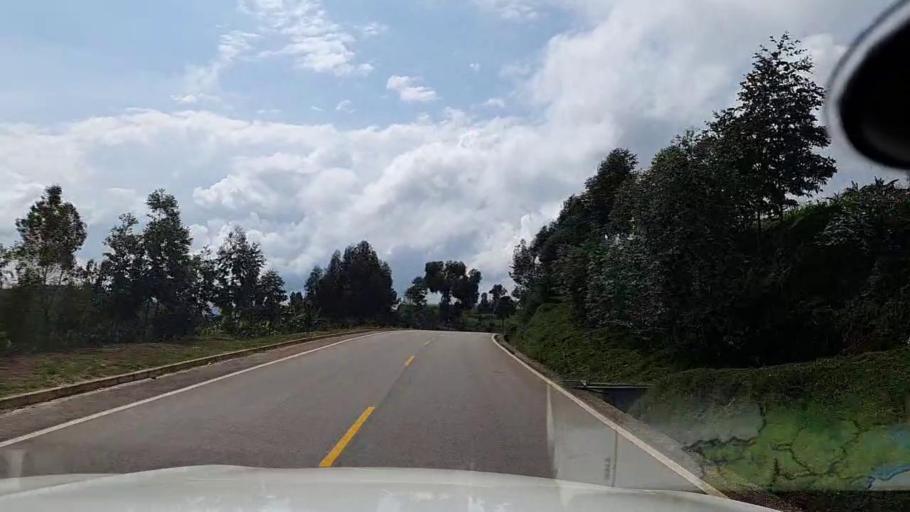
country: RW
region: Southern Province
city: Nzega
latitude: -2.4991
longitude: 29.5075
